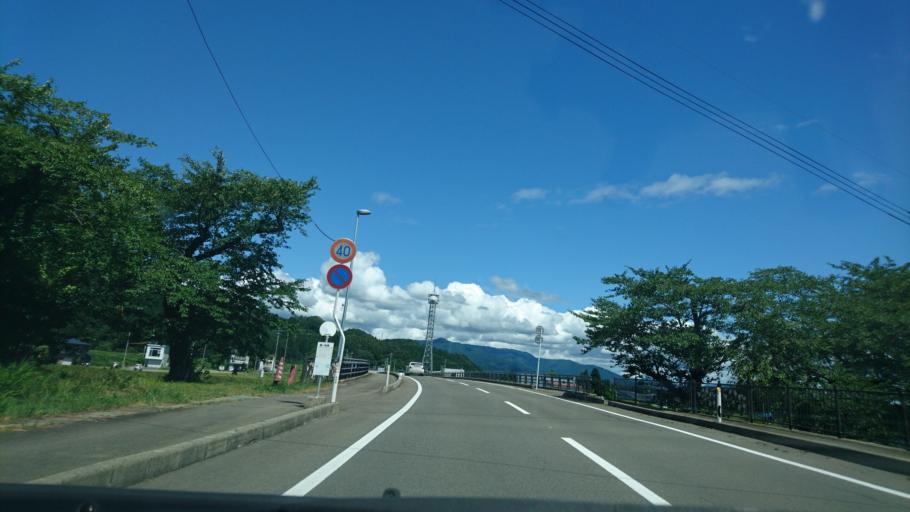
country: JP
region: Akita
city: Kakunodatemachi
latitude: 39.6055
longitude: 140.5585
